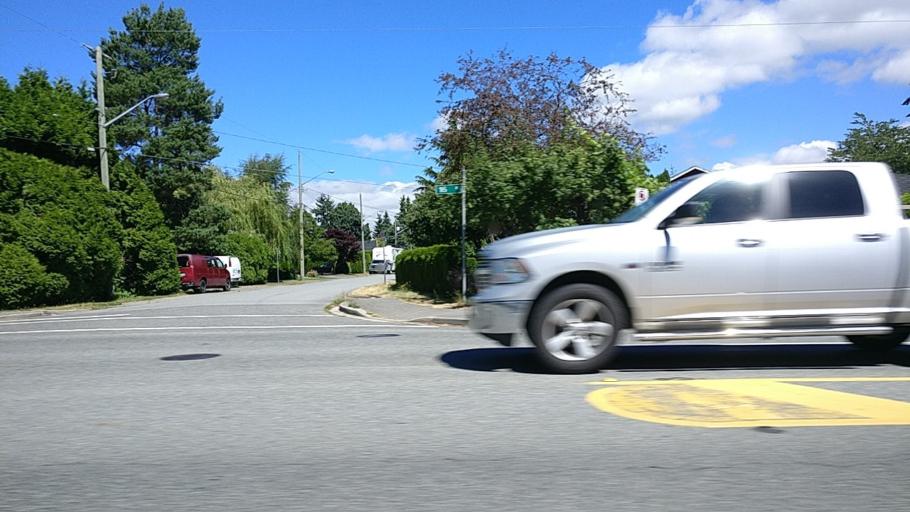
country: CA
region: British Columbia
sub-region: Greater Vancouver Regional District
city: White Rock
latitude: 49.0310
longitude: -122.7886
